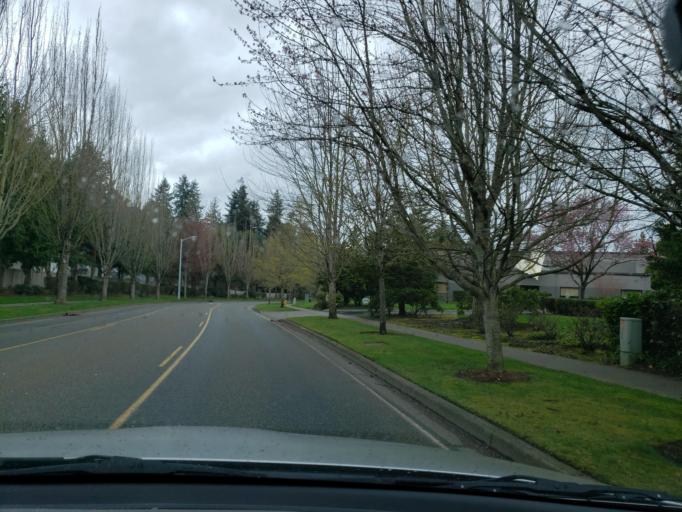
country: US
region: Washington
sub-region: Snohomish County
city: Mukilteo
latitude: 47.8921
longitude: -122.2979
